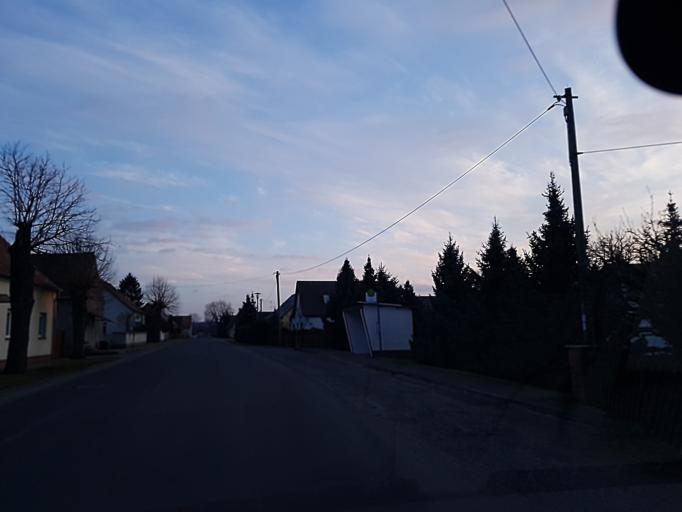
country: DE
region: Brandenburg
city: Herzberg
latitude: 51.7538
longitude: 13.2065
